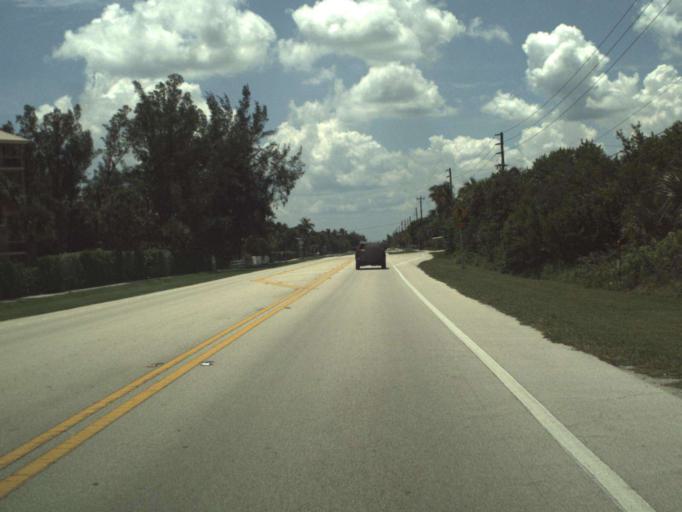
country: US
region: Florida
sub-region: Martin County
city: Sewall's Point
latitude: 27.2357
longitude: -80.1870
